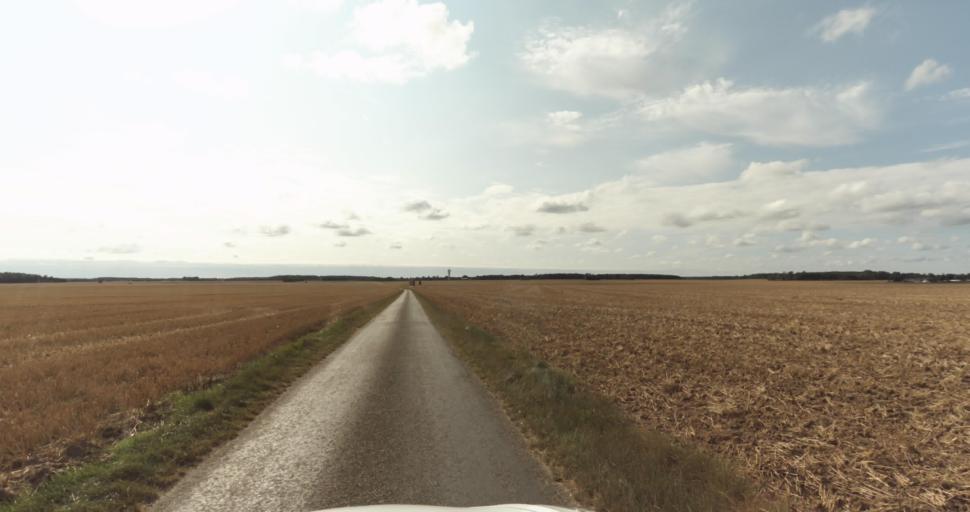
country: FR
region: Haute-Normandie
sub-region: Departement de l'Eure
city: Tillieres-sur-Avre
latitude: 48.7867
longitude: 1.0641
